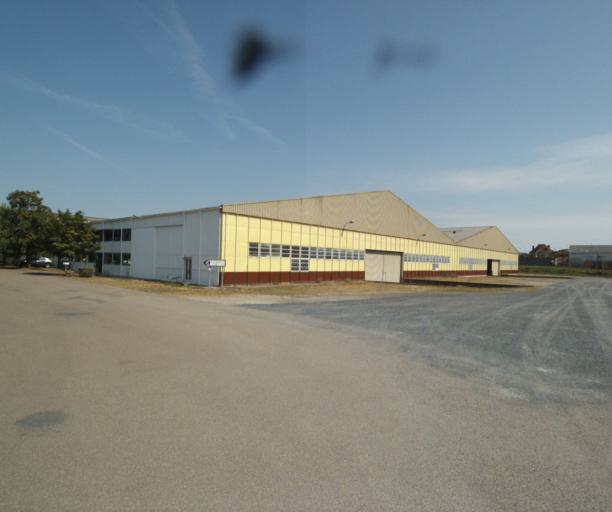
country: FR
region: Bourgogne
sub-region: Departement de Saone-et-Loire
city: Gueugnon
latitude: 46.5948
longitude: 4.0651
